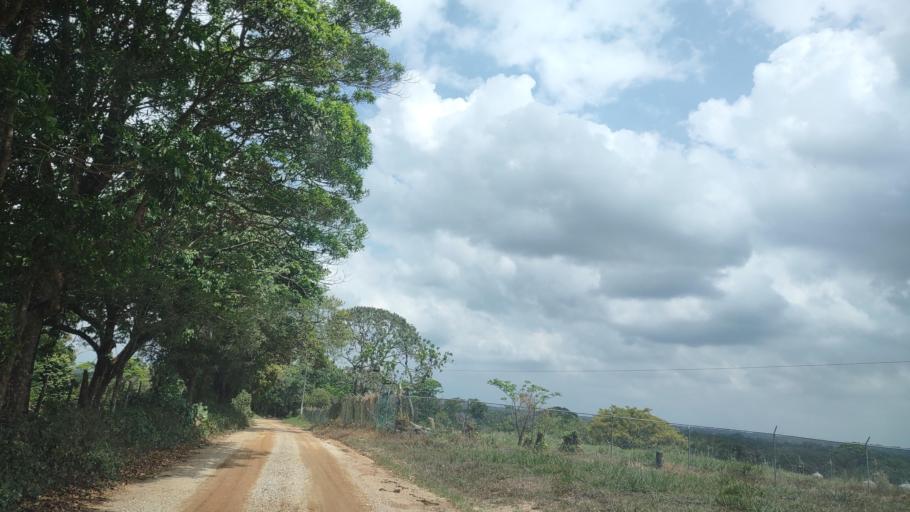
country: MX
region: Veracruz
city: Las Choapas
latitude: 17.9582
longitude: -94.1159
